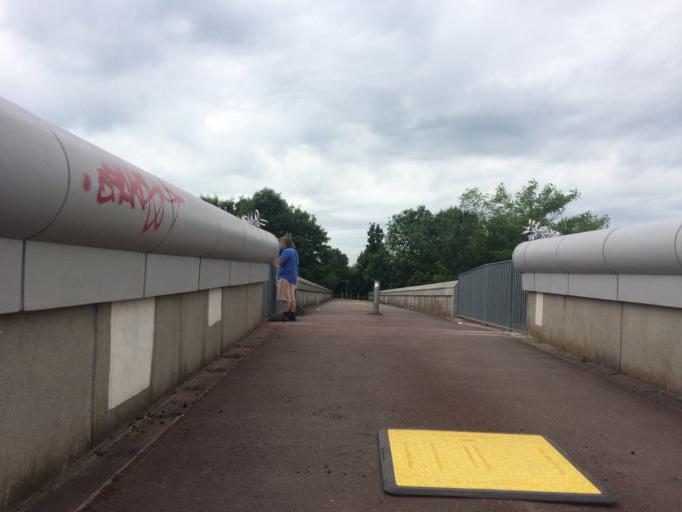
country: GB
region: England
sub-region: Milton Keynes
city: Loughton
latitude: 52.0333
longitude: -0.7740
